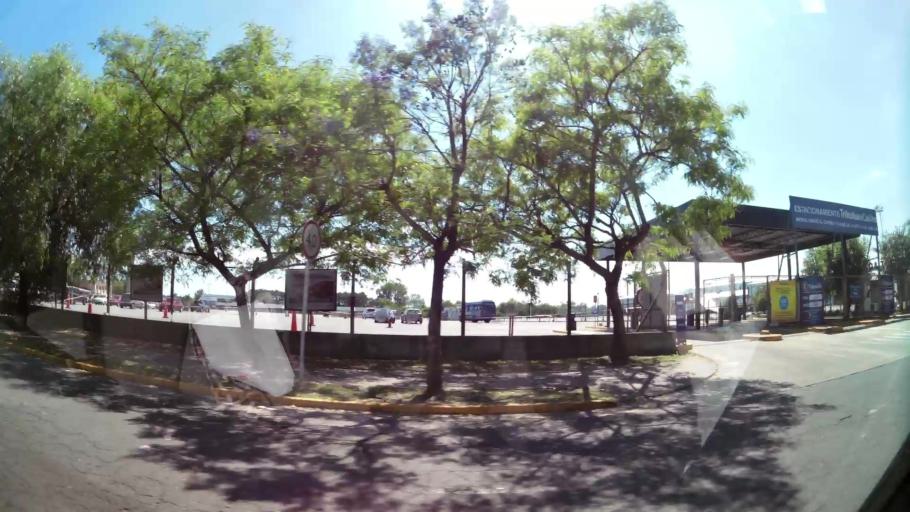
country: AR
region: Buenos Aires
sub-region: Partido de Tigre
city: Tigre
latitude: -34.4228
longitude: -58.5708
